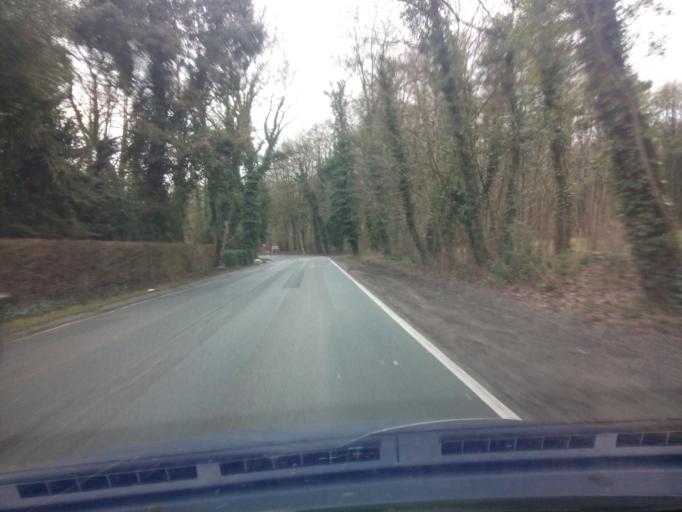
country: DE
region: Lower Saxony
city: Worpswede
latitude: 53.2182
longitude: 8.9340
